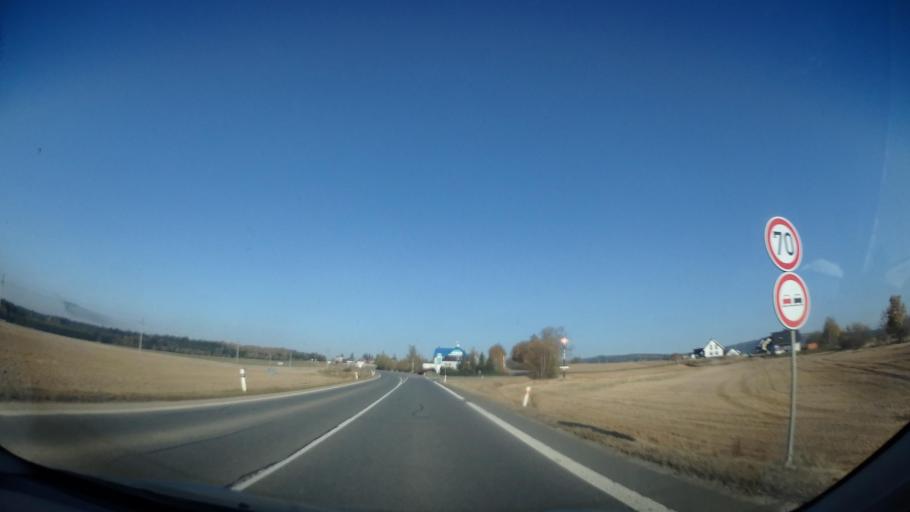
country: CZ
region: Vysocina
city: Zd'ar nad Sazavou Druhy
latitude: 49.6265
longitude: 15.9276
